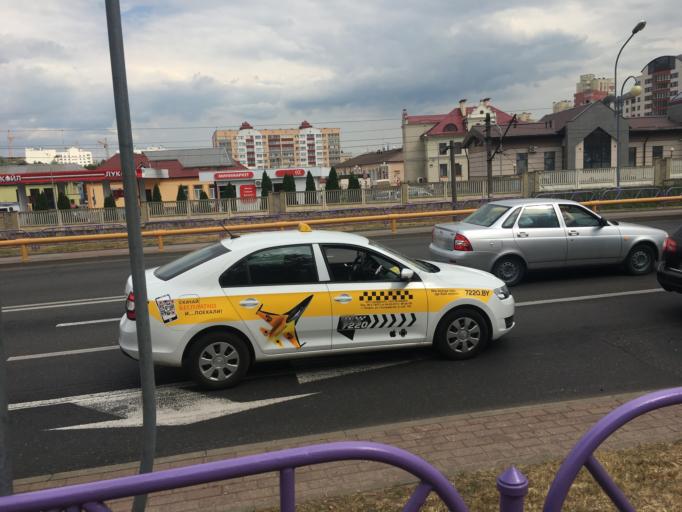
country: BY
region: Grodnenskaya
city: Hrodna
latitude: 53.6779
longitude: 23.8411
